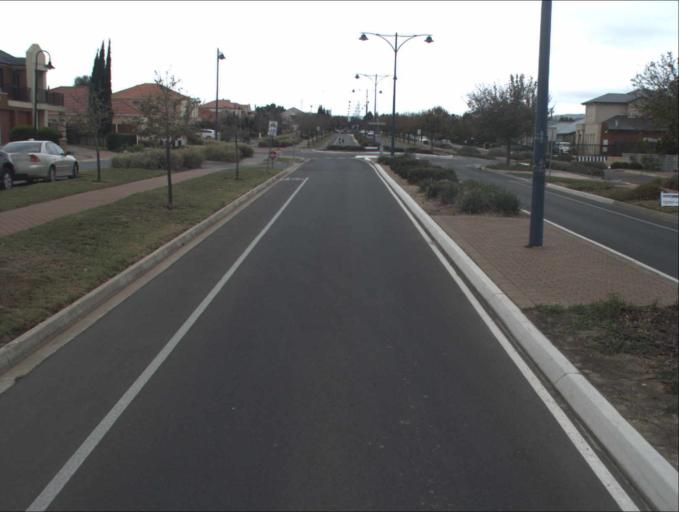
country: AU
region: South Australia
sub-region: Port Adelaide Enfield
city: Gilles Plains
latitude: -34.8581
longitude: 138.6297
